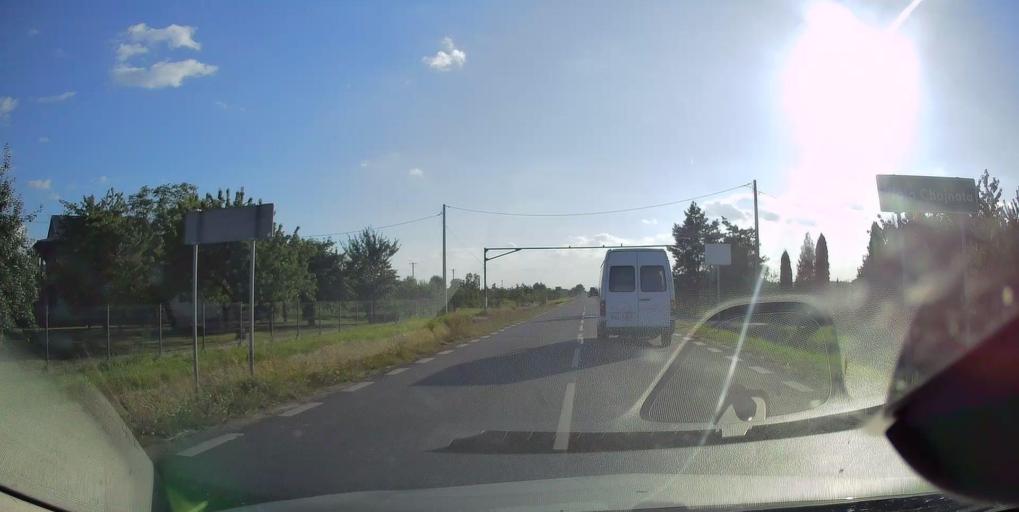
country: PL
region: Lodz Voivodeship
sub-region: Powiat rawski
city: Biala Rawska
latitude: 51.8035
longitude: 20.5503
